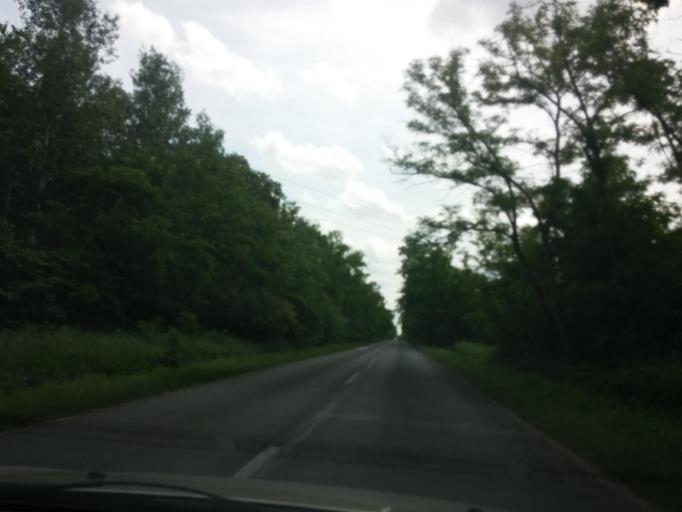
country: HU
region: Pest
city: Szigetcsep
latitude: 47.2927
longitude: 18.9812
